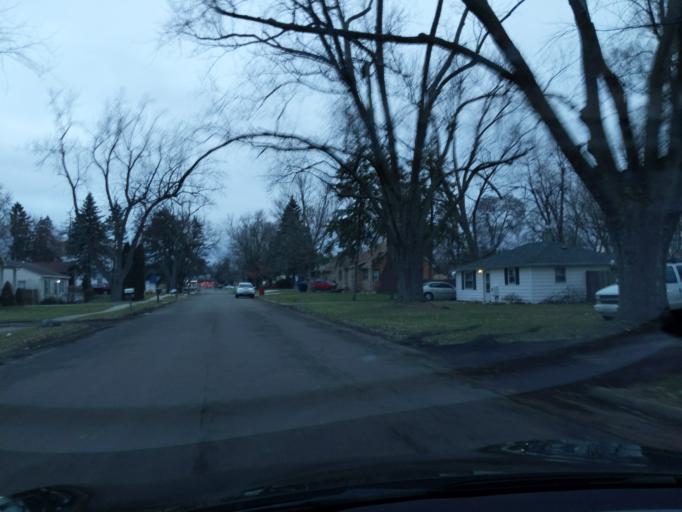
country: US
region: Michigan
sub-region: Eaton County
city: Waverly
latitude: 42.7390
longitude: -84.6170
